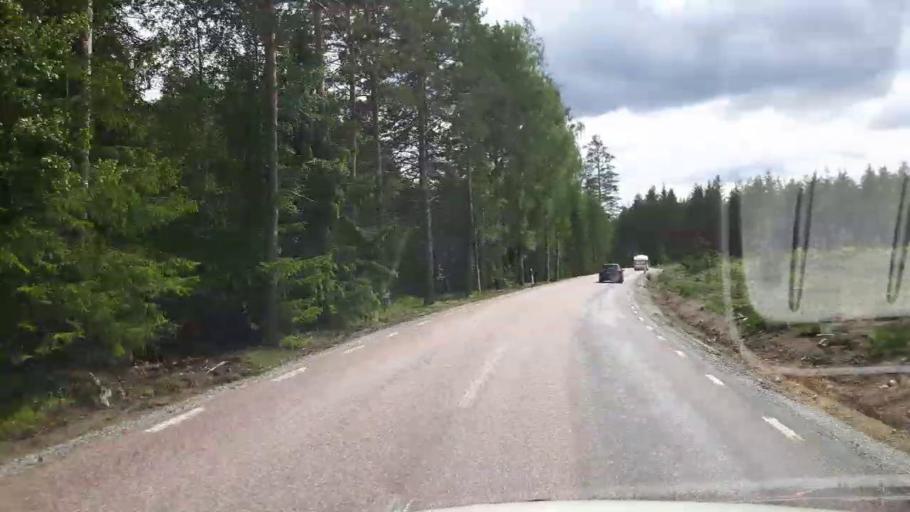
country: SE
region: Vaestmanland
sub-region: Skinnskattebergs Kommun
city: Skinnskatteberg
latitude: 59.8201
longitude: 15.8372
